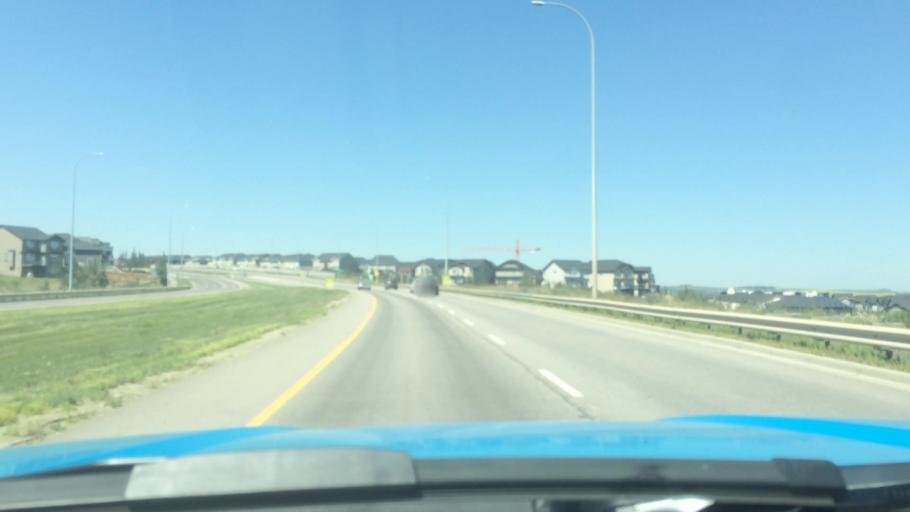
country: CA
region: Alberta
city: Calgary
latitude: 51.1607
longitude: -114.1415
